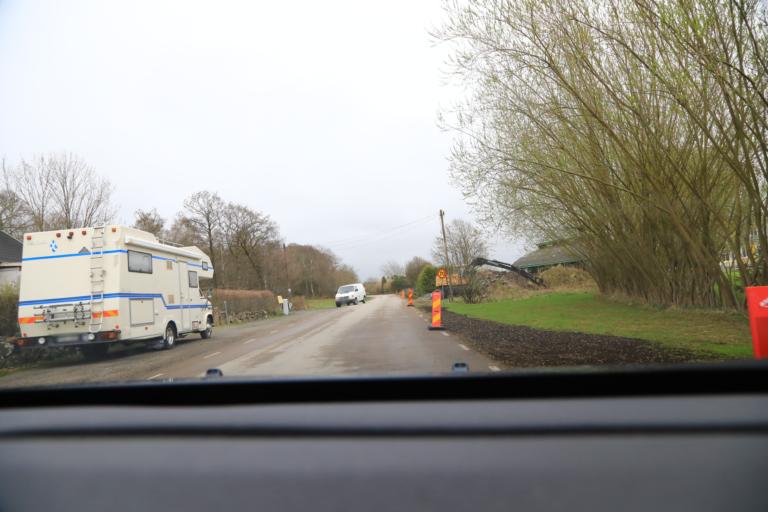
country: SE
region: Halland
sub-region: Kungsbacka Kommun
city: Frillesas
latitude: 57.2993
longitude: 12.1810
